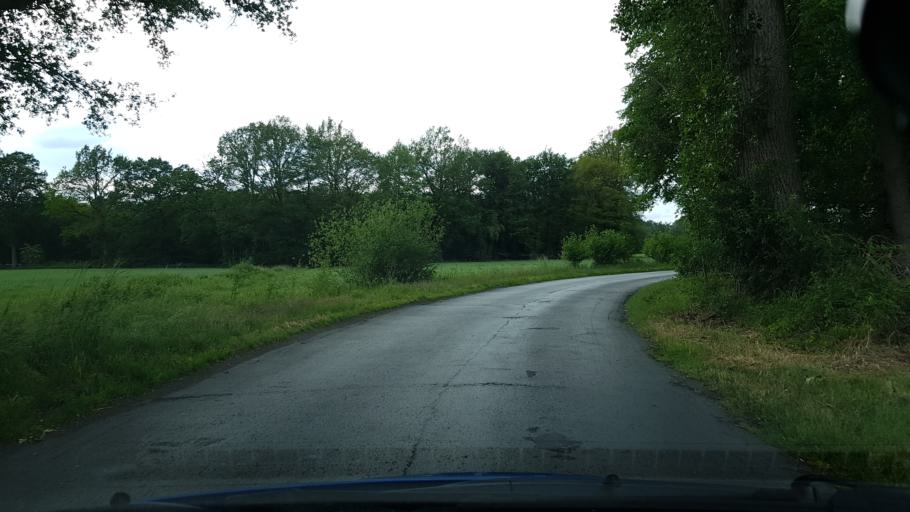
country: DE
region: North Rhine-Westphalia
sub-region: Regierungsbezirk Munster
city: Steinfurt
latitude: 52.1243
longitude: 7.3544
